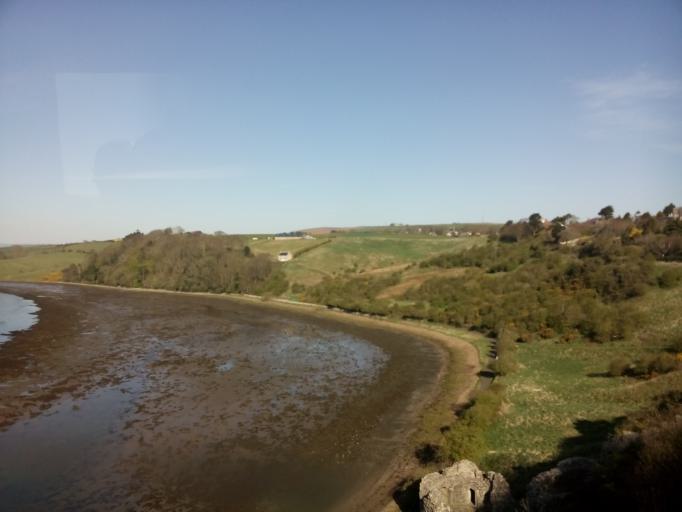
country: GB
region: England
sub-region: Northumberland
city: Berwick-Upon-Tweed
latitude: 55.7732
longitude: -2.0123
